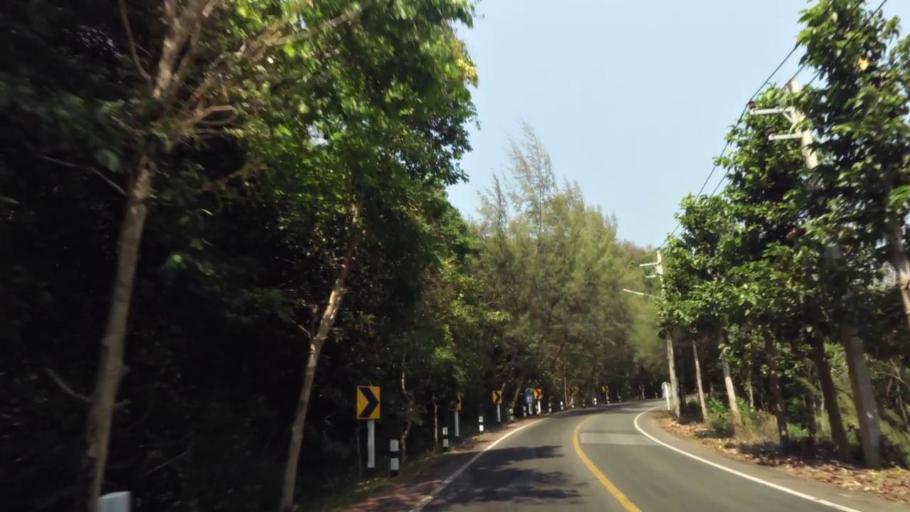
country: TH
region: Chanthaburi
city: Tha Mai
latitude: 12.5254
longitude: 101.9479
